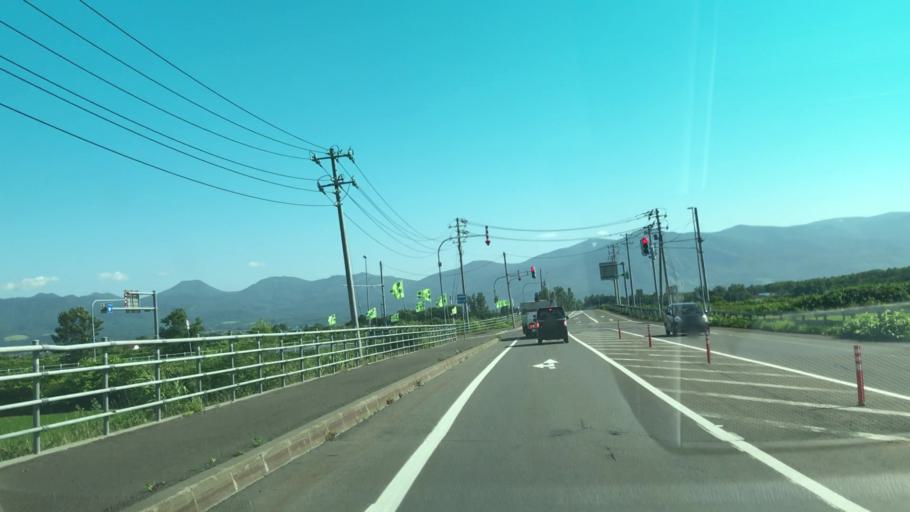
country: JP
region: Hokkaido
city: Iwanai
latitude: 43.0246
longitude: 140.5487
